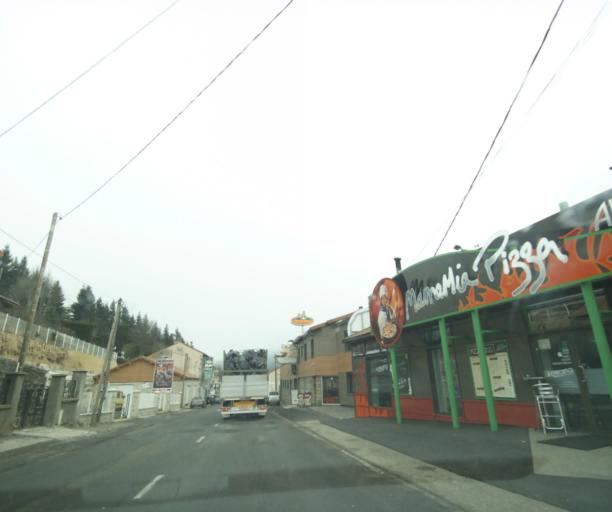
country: FR
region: Languedoc-Roussillon
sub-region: Departement de la Lozere
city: Langogne
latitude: 44.7293
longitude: 4.0053
